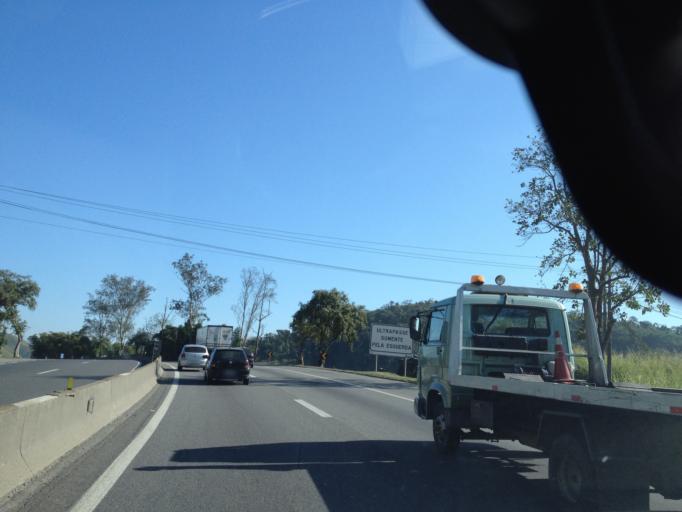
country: BR
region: Rio de Janeiro
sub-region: Porto Real
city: Porto Real
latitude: -22.4876
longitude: -44.2464
